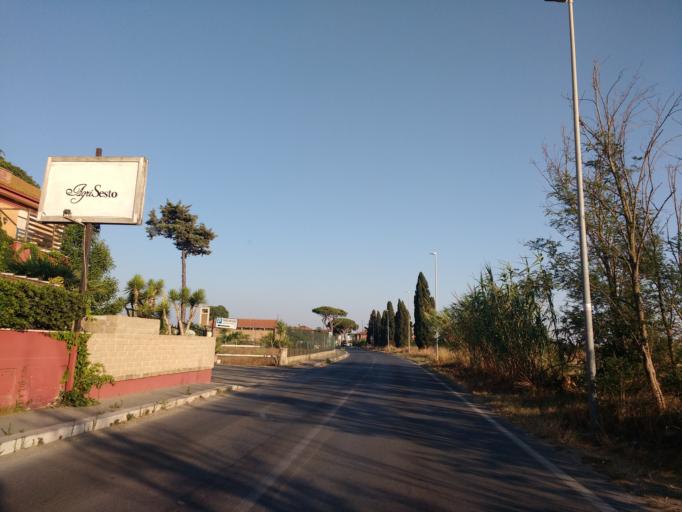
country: IT
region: Latium
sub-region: Citta metropolitana di Roma Capitale
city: Focene
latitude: 41.8357
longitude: 12.2300
